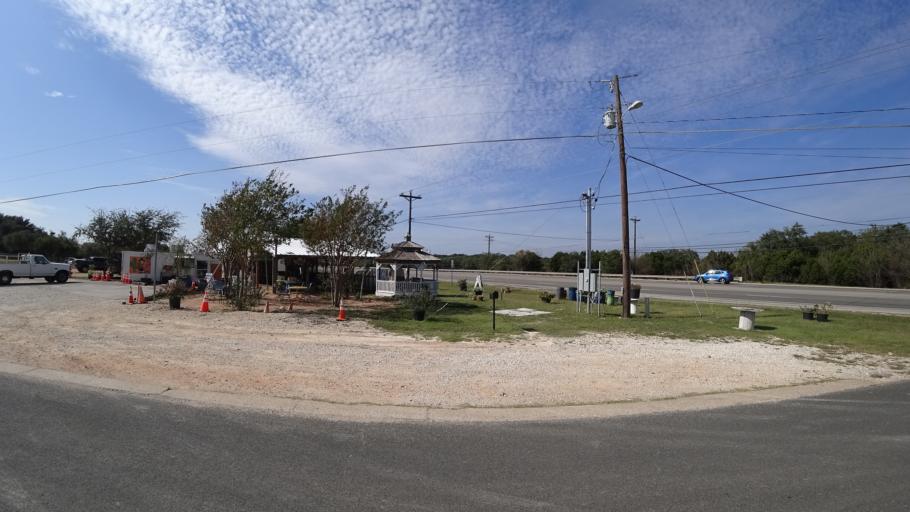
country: US
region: Texas
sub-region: Travis County
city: Bee Cave
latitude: 30.2300
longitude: -97.9350
